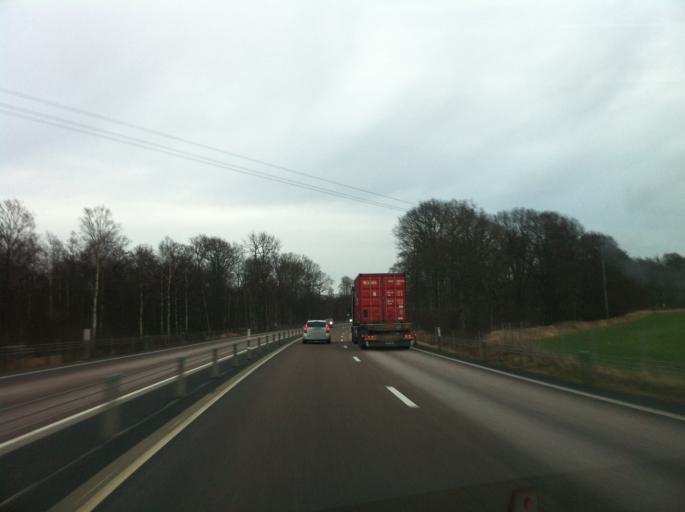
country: SE
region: Skane
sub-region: Helsingborg
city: Helsingborg
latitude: 56.1090
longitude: 12.6511
